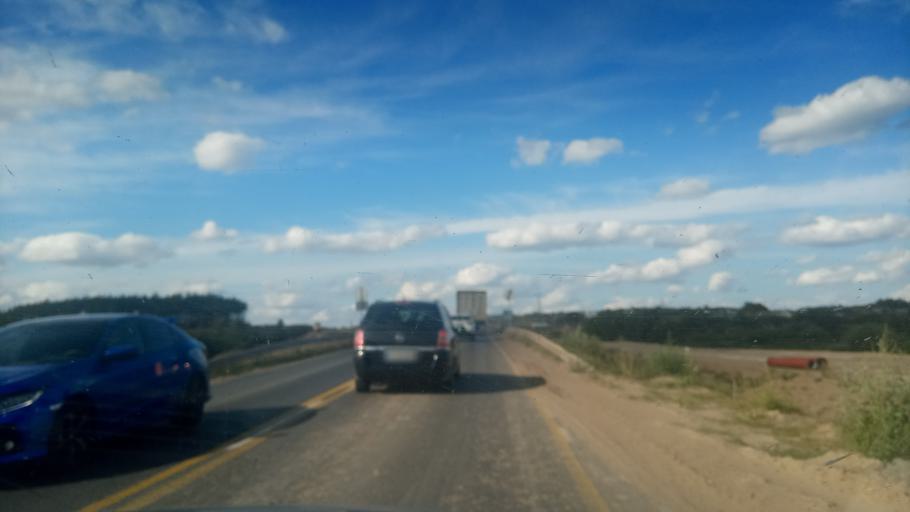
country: PL
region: Kujawsko-Pomorskie
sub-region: Powiat bydgoski
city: Biale Blota
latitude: 53.1496
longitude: 17.8845
